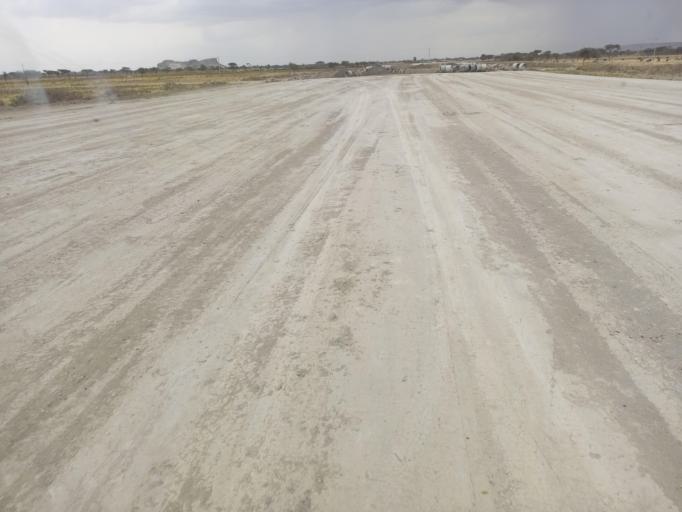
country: ET
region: Oromiya
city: Ziway
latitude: 7.8684
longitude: 38.6715
